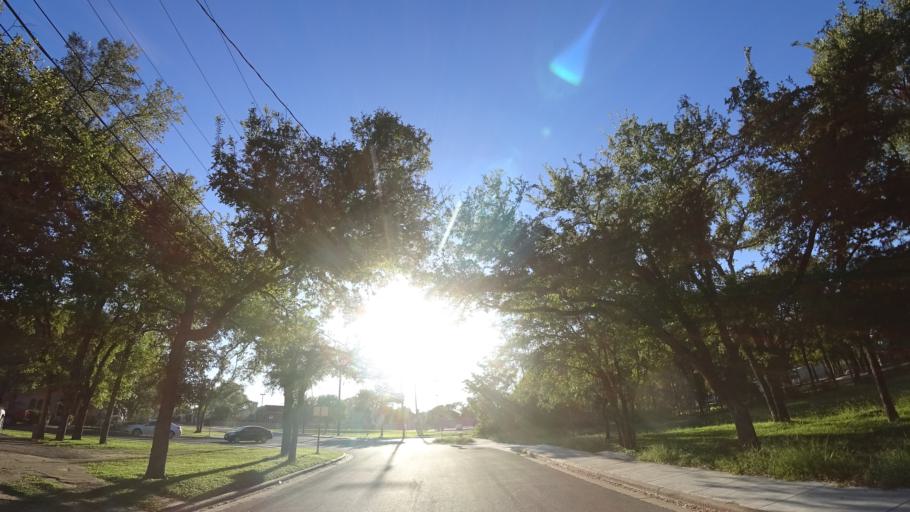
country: US
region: Texas
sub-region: Travis County
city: Austin
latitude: 30.2366
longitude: -97.7010
